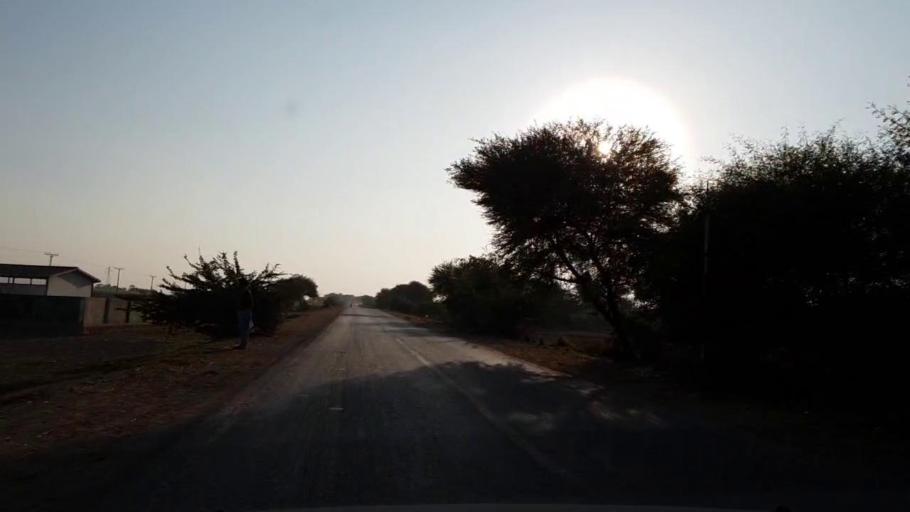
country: PK
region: Sindh
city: Daro Mehar
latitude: 24.6595
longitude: 68.1326
